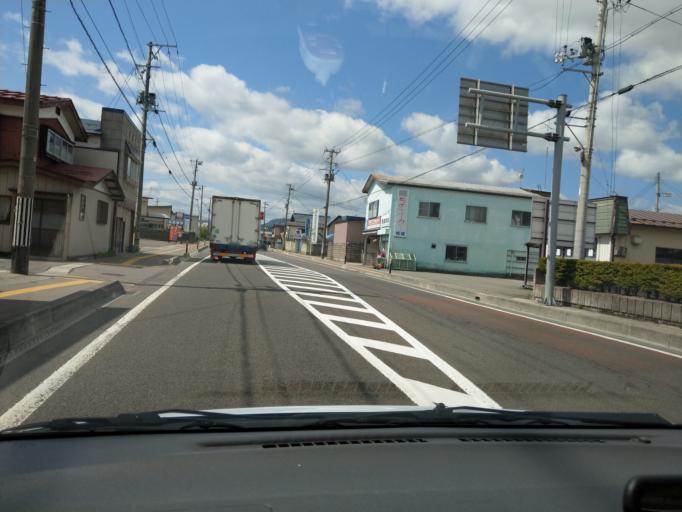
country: JP
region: Akita
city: Yuzawa
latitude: 39.1733
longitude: 140.4917
